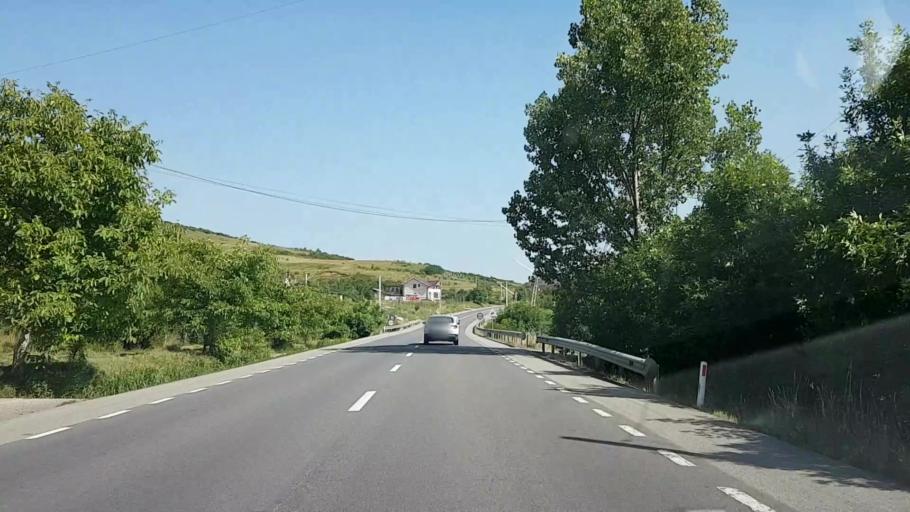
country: RO
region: Bistrita-Nasaud
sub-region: Comuna Sieu-Magherus
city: Sieu-Magherus
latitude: 47.0789
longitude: 24.3949
